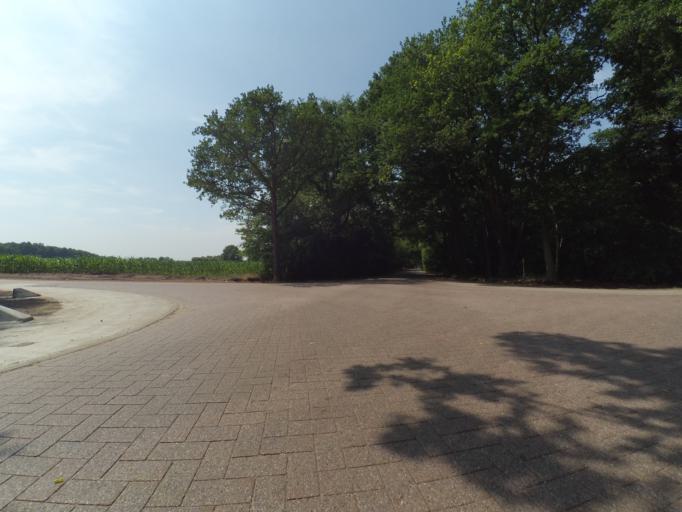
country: NL
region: North Brabant
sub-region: Gemeente Zundert
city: Zundert
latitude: 51.4459
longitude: 4.6906
